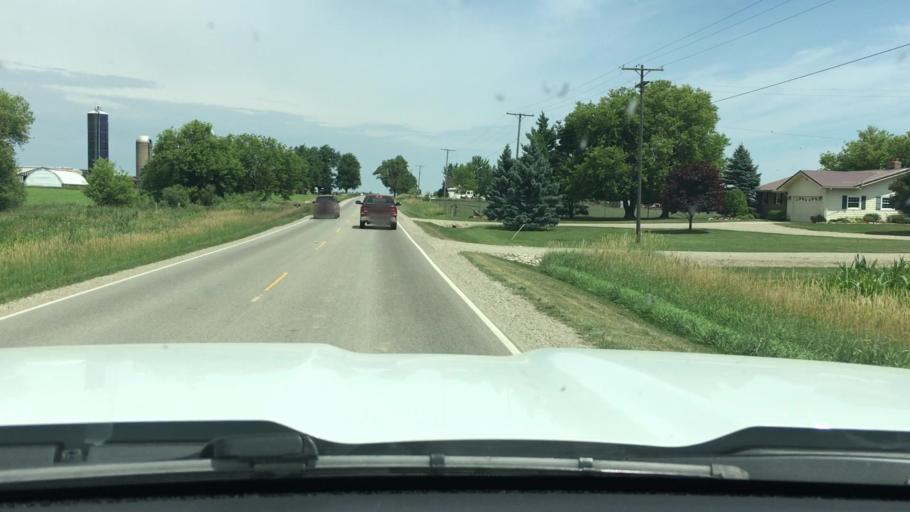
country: US
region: Michigan
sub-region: Sanilac County
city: Brown City
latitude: 43.2737
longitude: -82.9824
